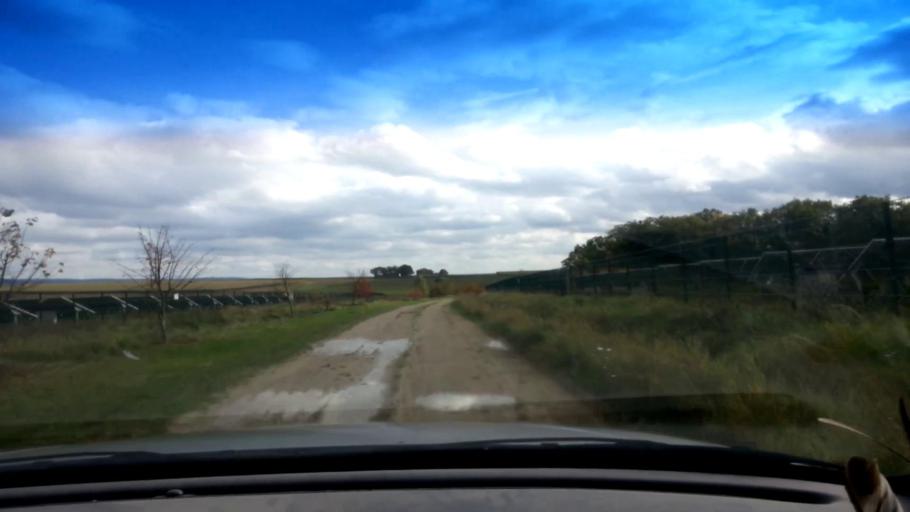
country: DE
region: Bavaria
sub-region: Upper Franconia
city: Zapfendorf
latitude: 49.9806
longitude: 10.9635
